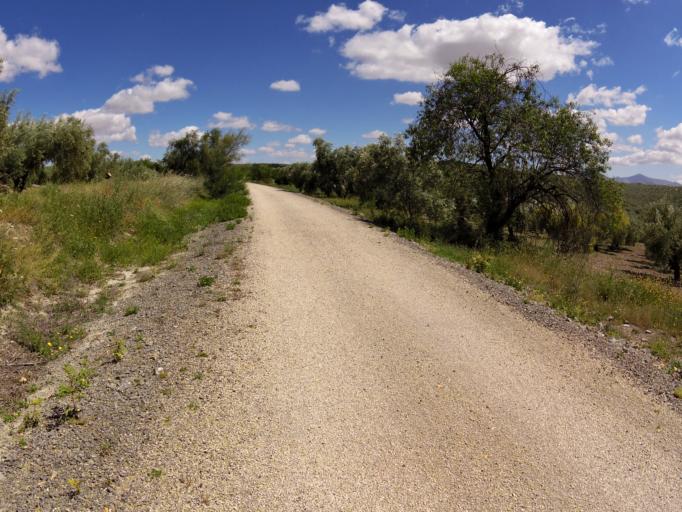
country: ES
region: Andalusia
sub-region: Provincia de Jaen
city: Alcaudete
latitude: 37.6513
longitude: -4.0619
